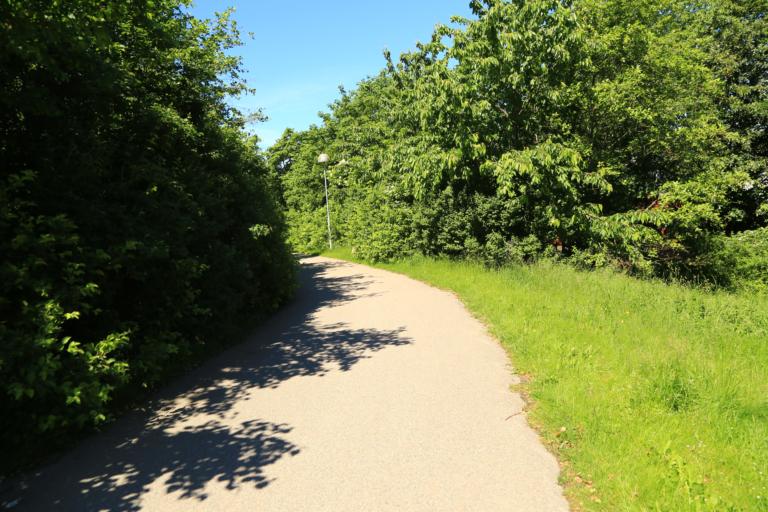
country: SE
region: Halland
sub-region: Varbergs Kommun
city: Varberg
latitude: 57.1027
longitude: 12.2696
